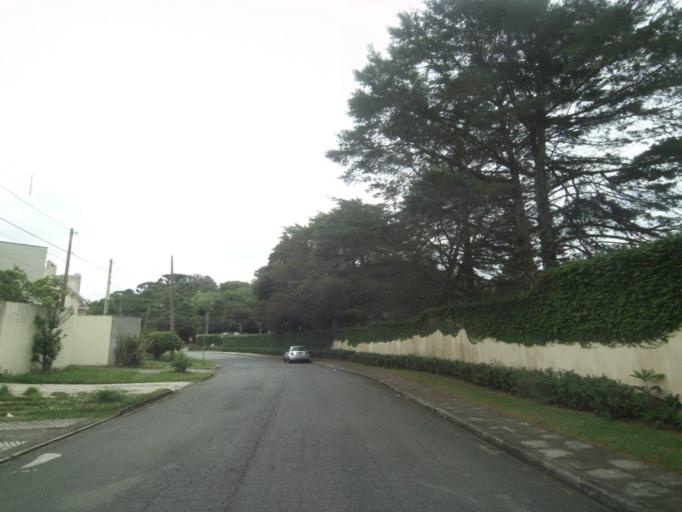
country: BR
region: Parana
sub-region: Curitiba
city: Curitiba
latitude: -25.4008
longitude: -49.2936
